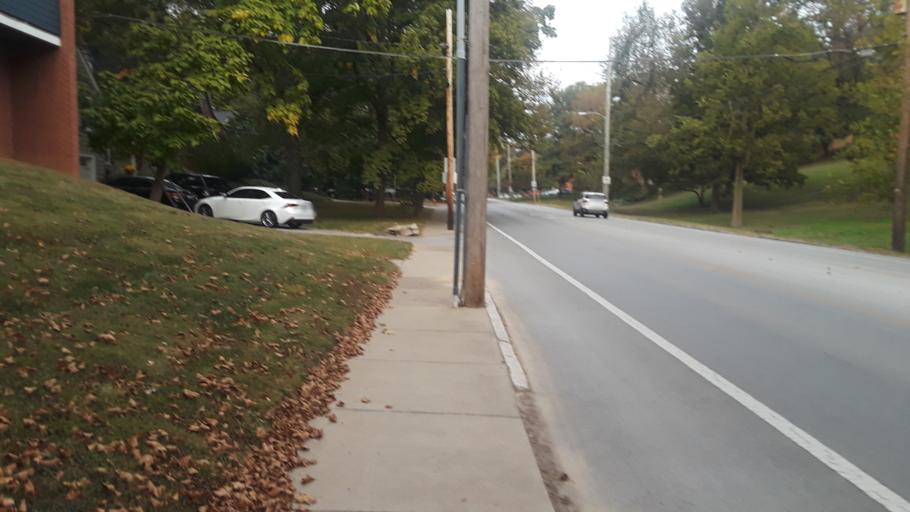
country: US
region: Kentucky
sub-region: Jefferson County
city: Saint Matthews
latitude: 38.2502
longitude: -85.6893
